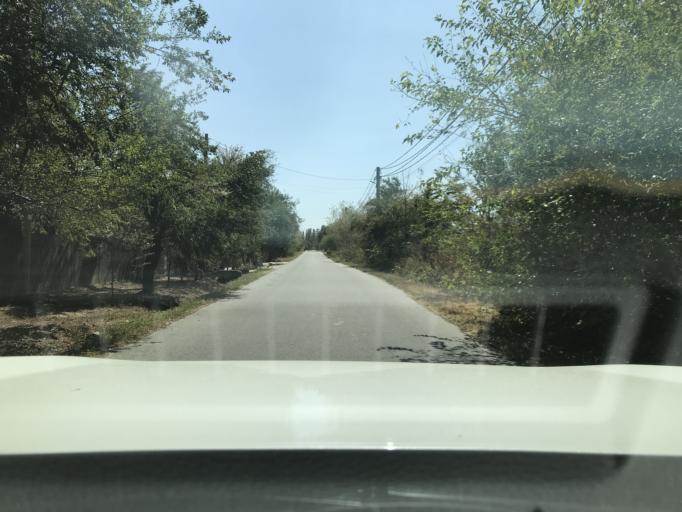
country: RO
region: Olt
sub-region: Comuna Falcoiu
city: Falcoiu
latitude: 44.2413
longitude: 24.3662
